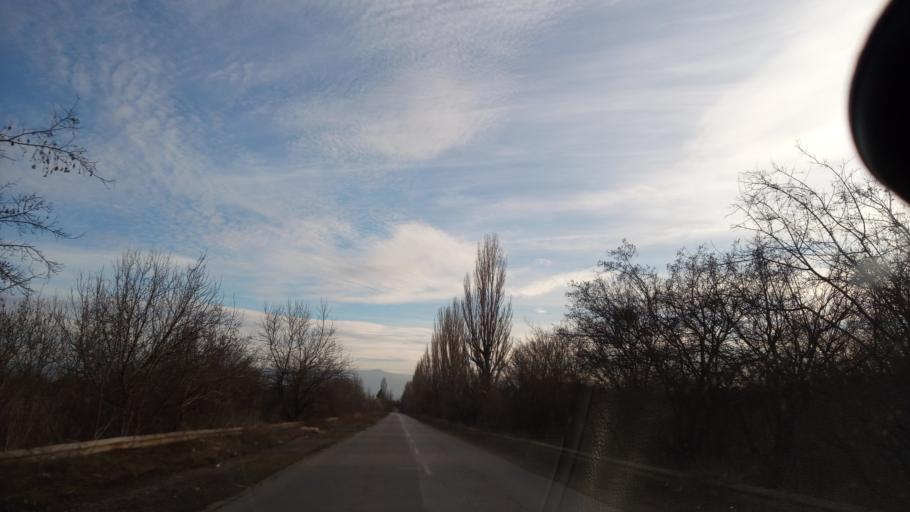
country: BG
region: Sofia-Capital
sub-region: Stolichna Obshtina
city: Bukhovo
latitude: 42.7400
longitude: 23.5549
